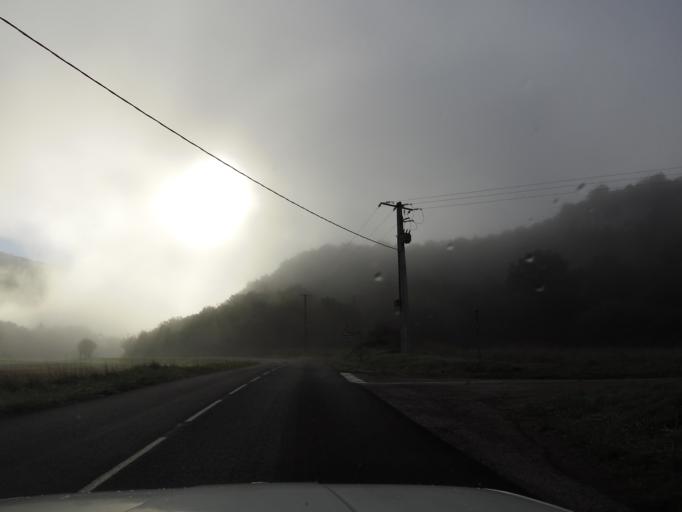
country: FR
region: Rhone-Alpes
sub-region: Departement de l'Isere
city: Creys-Mepieu
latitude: 45.7604
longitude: 5.4908
